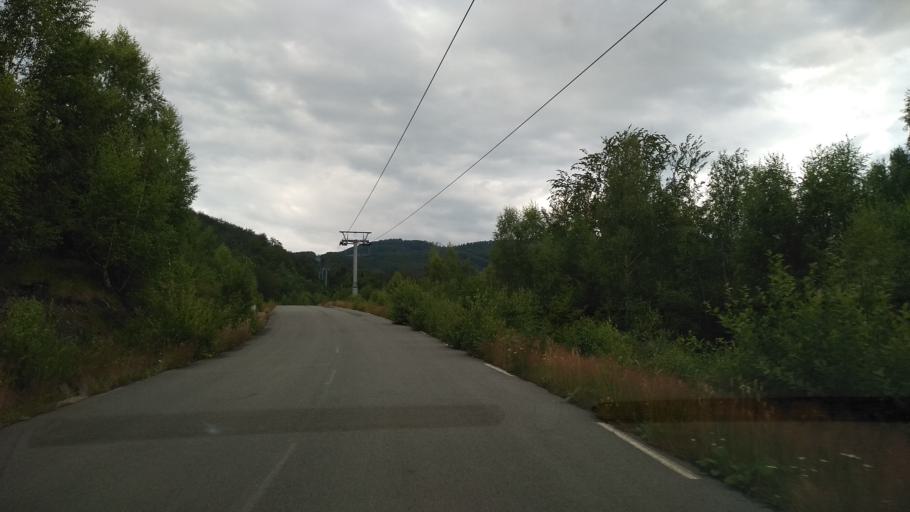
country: RO
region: Hunedoara
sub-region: Municipiul  Vulcan
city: Jiu-Paroseni
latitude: 45.3508
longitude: 23.2898
